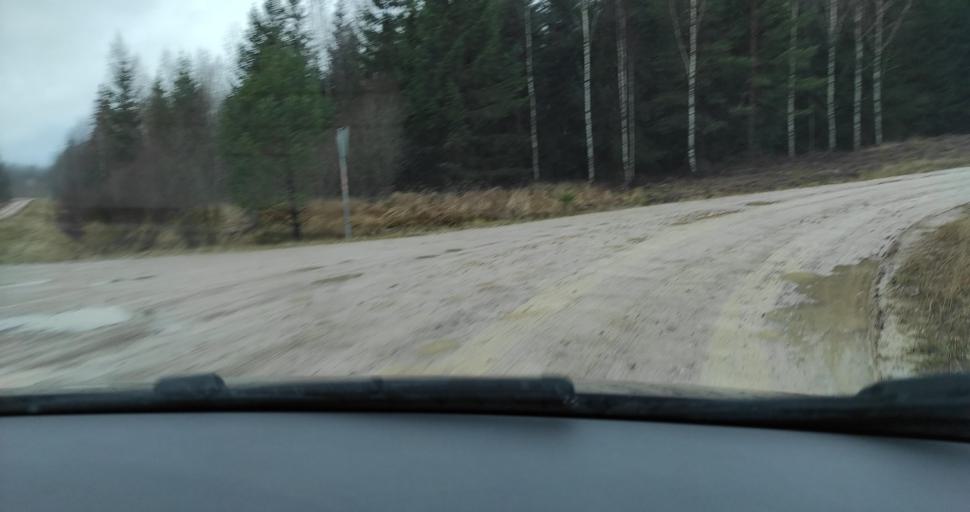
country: LV
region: Skrunda
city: Skrunda
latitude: 56.5548
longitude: 22.0823
